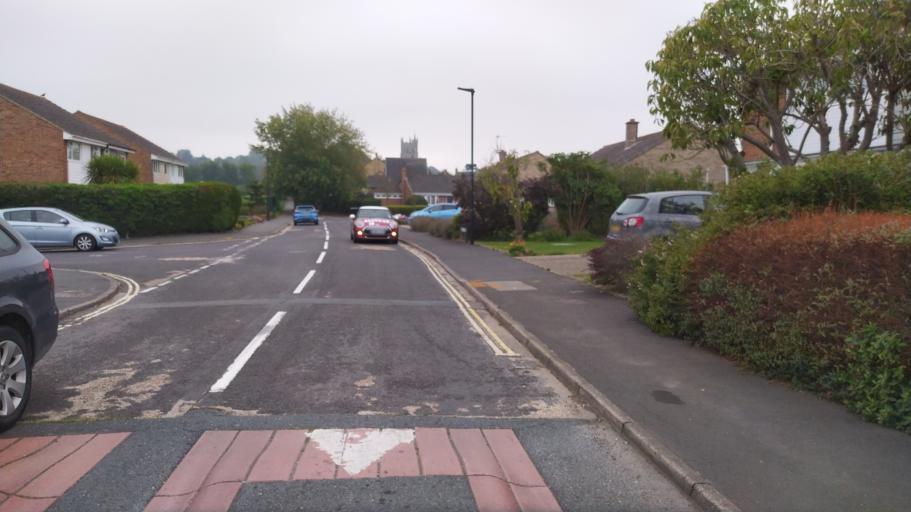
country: GB
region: England
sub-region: Isle of Wight
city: Newport
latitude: 50.6948
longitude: -1.3137
